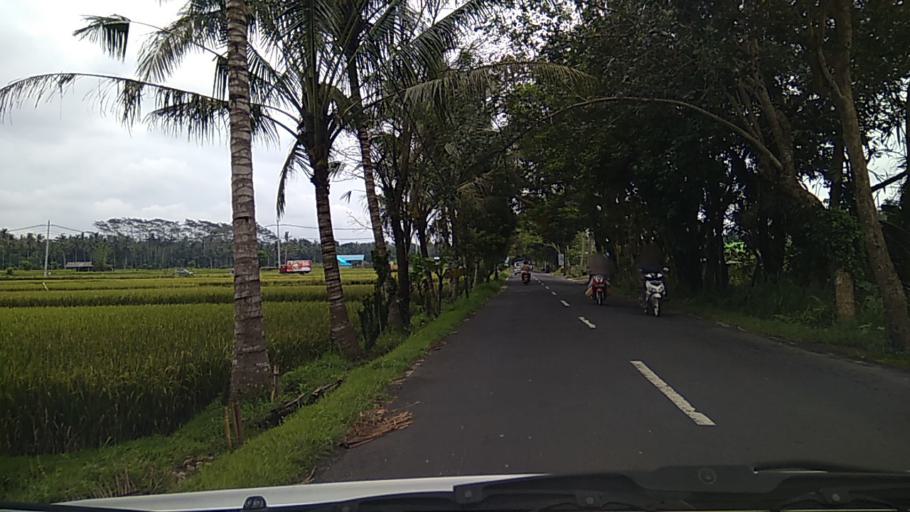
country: ID
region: Bali
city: Brahmana
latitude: -8.4778
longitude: 115.2080
